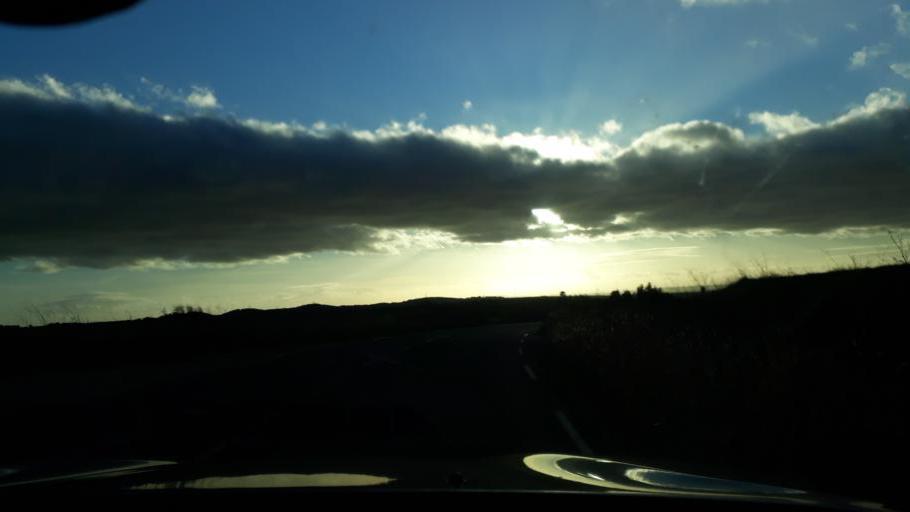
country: FR
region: Languedoc-Roussillon
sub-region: Departement de l'Herault
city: Colombiers
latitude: 43.3051
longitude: 3.1371
